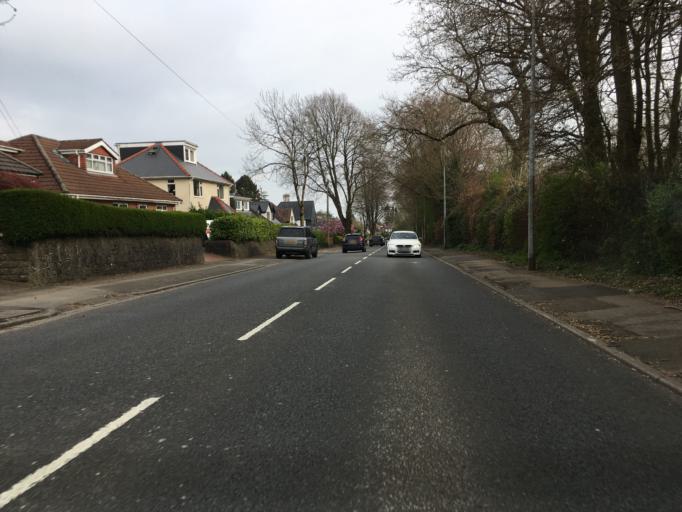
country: GB
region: Wales
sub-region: Cardiff
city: Radyr
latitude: 51.5304
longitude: -3.2235
